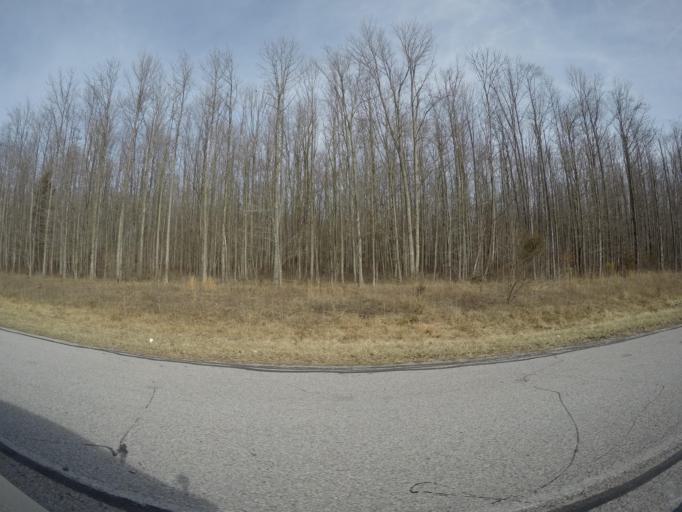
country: US
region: Maryland
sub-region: Cecil County
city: Perryville
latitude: 39.5696
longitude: -76.0655
